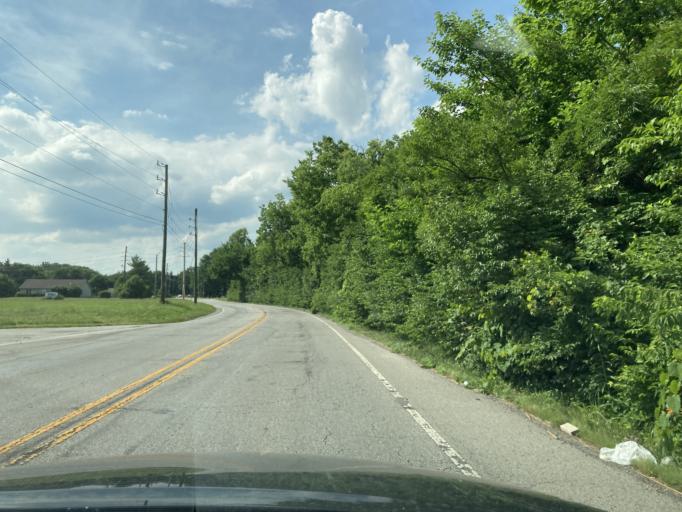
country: US
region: Indiana
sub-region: Marion County
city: Speedway
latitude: 39.8359
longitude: -86.2279
